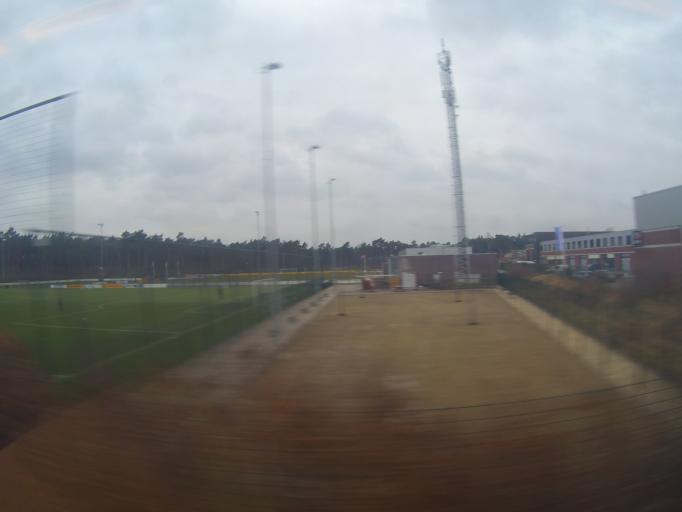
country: NL
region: Utrecht
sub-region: Gemeente Zeist
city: Zeist
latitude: 52.1376
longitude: 5.2323
